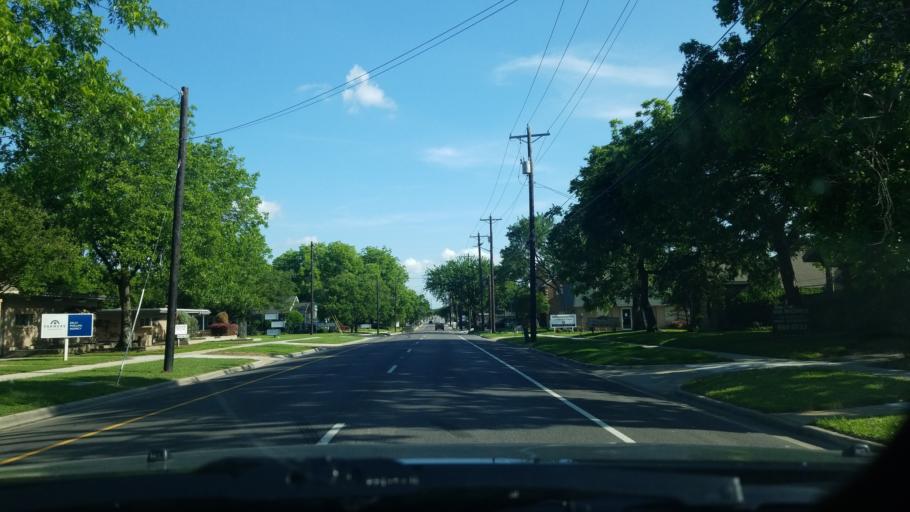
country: US
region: Texas
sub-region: Denton County
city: Denton
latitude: 33.2238
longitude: -97.1336
